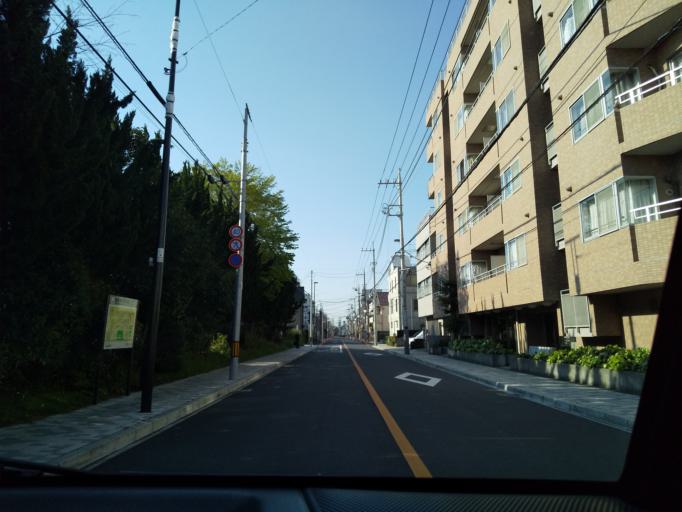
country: JP
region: Tokyo
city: Kokubunji
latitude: 35.6936
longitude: 139.4524
